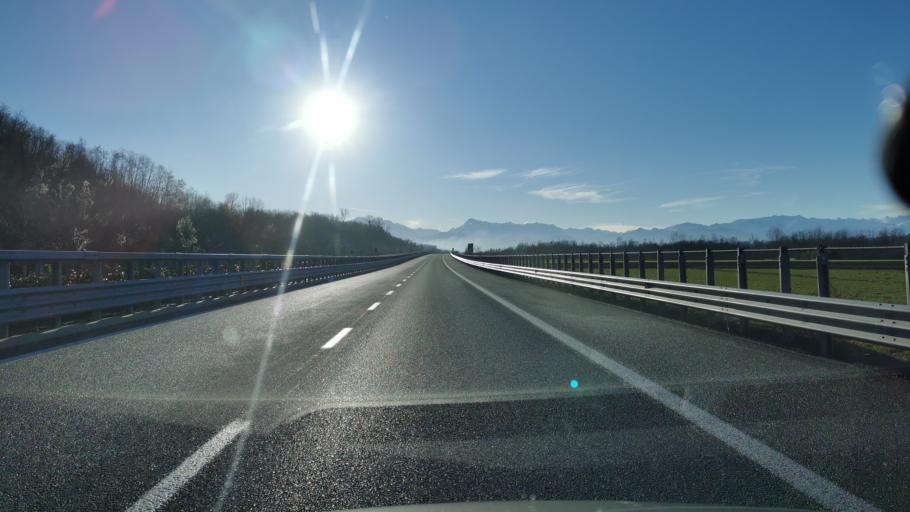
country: IT
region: Piedmont
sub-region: Provincia di Cuneo
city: Montanera
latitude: 44.4562
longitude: 7.6530
